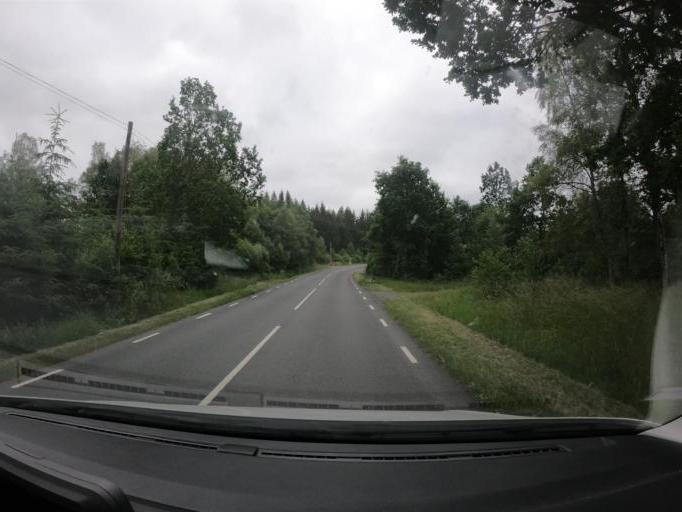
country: SE
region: Skane
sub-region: Perstorps Kommun
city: Perstorp
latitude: 56.1516
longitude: 13.3500
